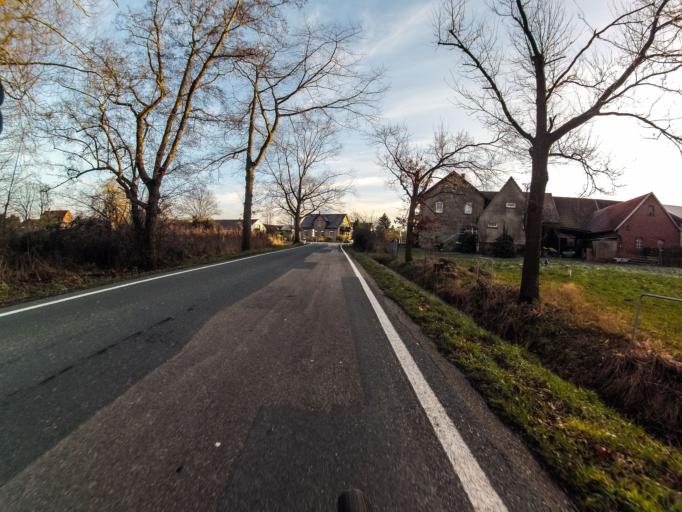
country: DE
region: North Rhine-Westphalia
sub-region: Regierungsbezirk Munster
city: Mettingen
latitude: 52.2968
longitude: 7.8233
